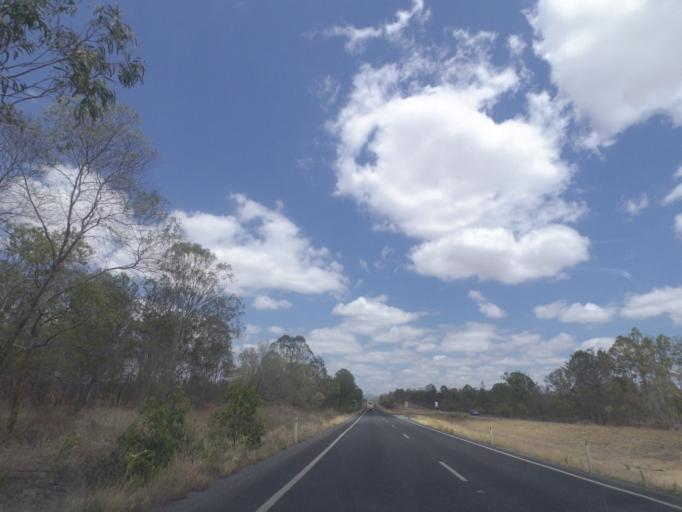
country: AU
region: Queensland
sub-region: Lockyer Valley
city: Gatton
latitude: -27.5517
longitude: 152.1464
